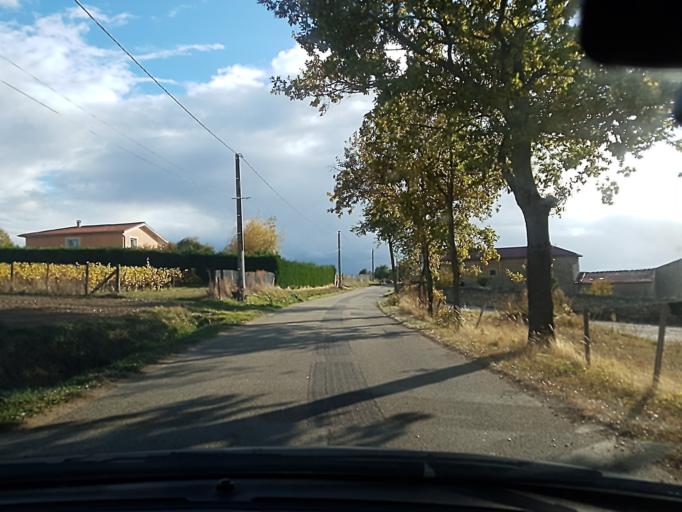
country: FR
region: Rhone-Alpes
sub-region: Departement du Rhone
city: Taluyers
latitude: 45.6322
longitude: 4.7180
